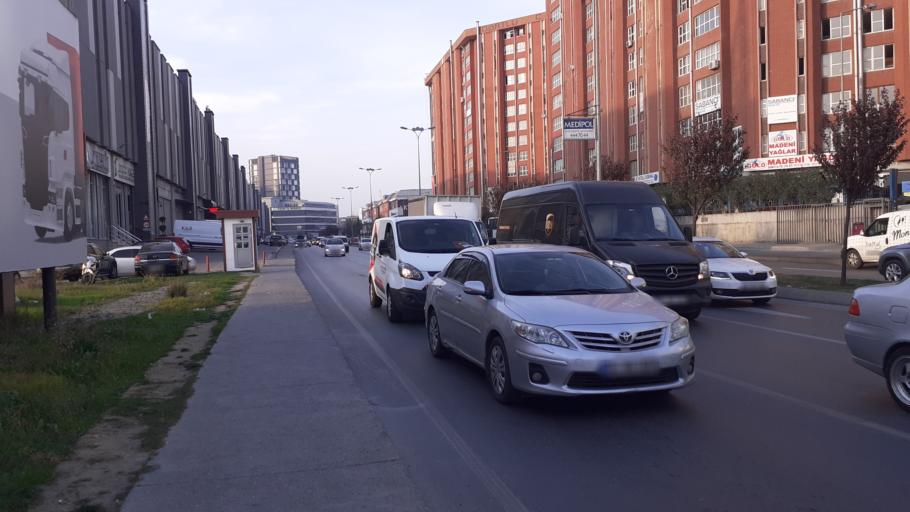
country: TR
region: Istanbul
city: Basaksehir
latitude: 41.0697
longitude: 28.7962
